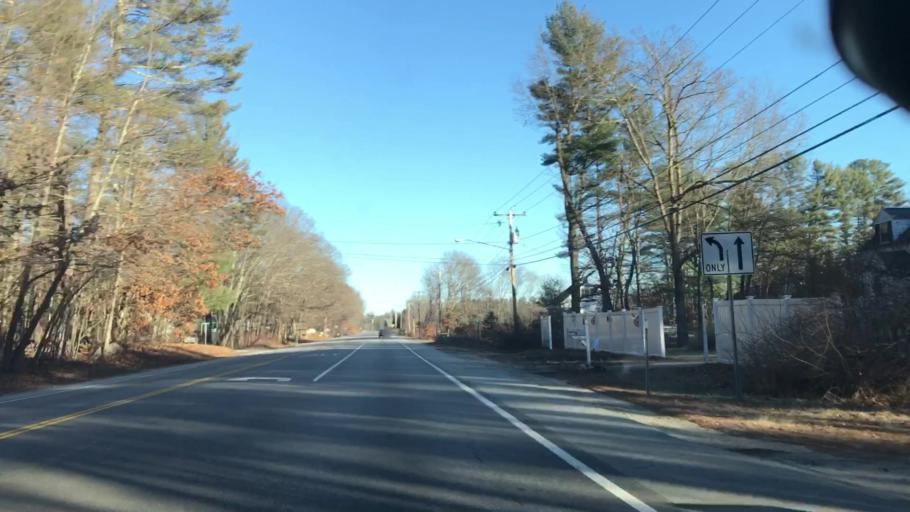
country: US
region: New Hampshire
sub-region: Hillsborough County
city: Mont Vernon
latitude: 42.8988
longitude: -71.5890
